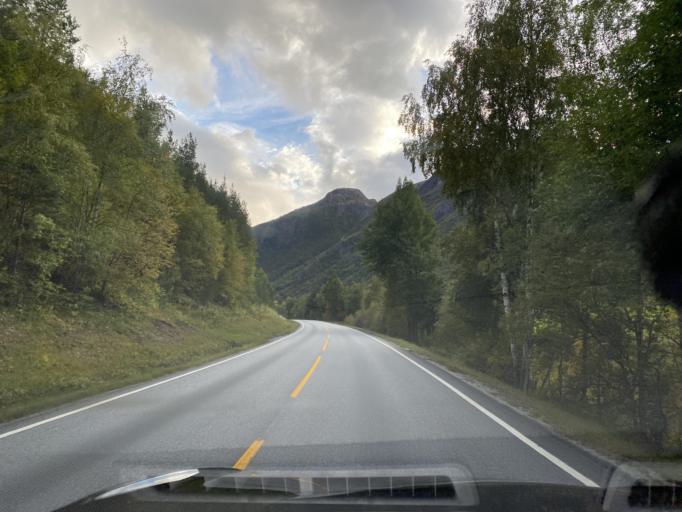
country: NO
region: Oppland
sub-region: Lom
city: Fossbergom
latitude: 61.8082
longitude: 8.4598
